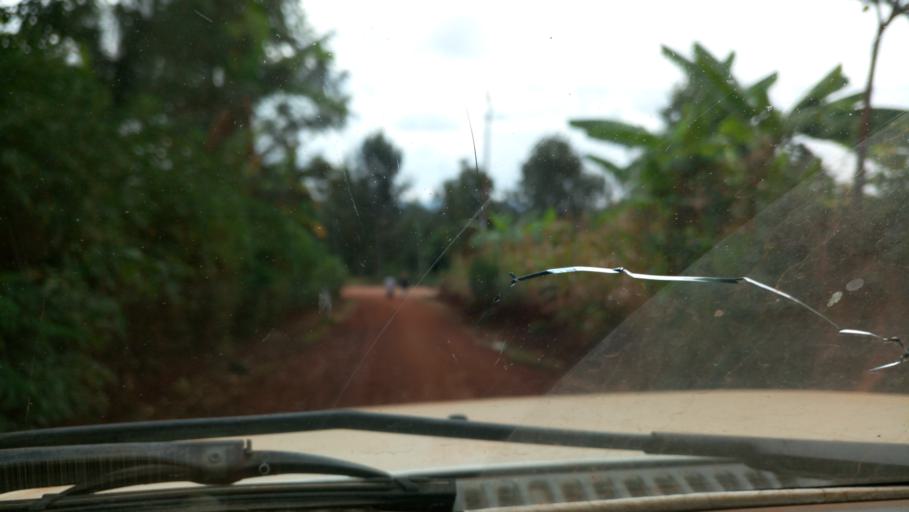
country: KE
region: Murang'a District
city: Maragua
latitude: -0.8486
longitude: 37.0971
